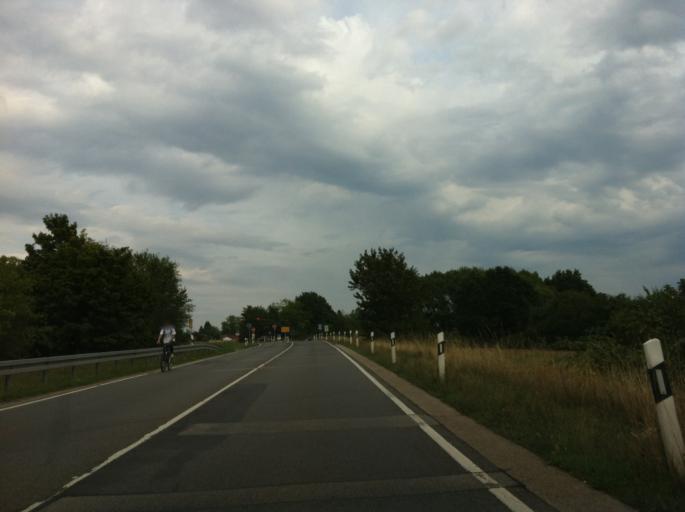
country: DE
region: Hesse
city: Schwalbach am Taunus
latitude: 50.1580
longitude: 8.5350
